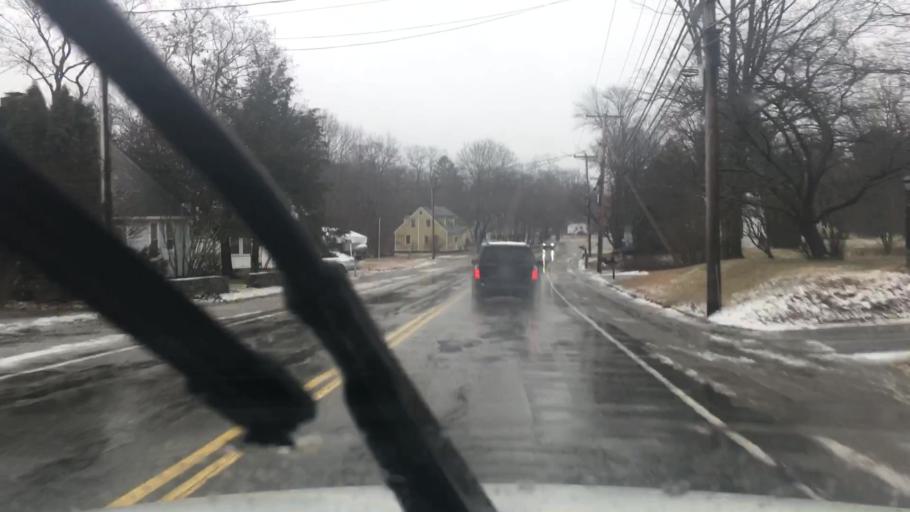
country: US
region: Maine
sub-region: York County
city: Saco
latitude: 43.4833
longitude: -70.4337
